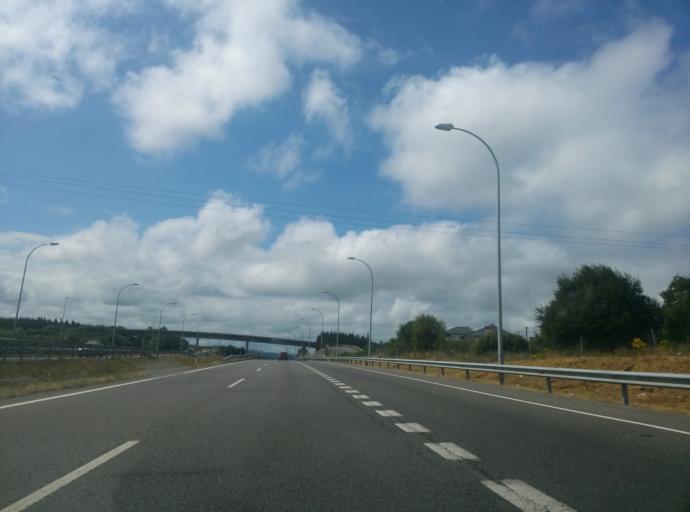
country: ES
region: Galicia
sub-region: Provincia de Lugo
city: Lugo
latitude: 43.0586
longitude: -7.5603
